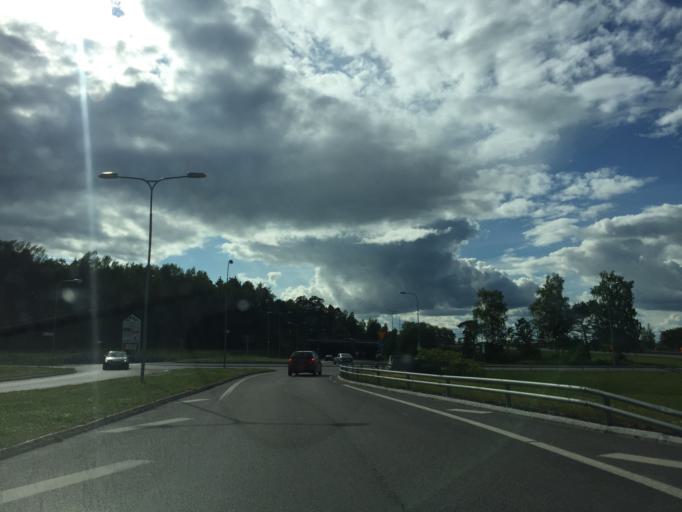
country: SE
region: Vaestmanland
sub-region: Vasteras
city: Vasteras
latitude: 59.6183
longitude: 16.5200
